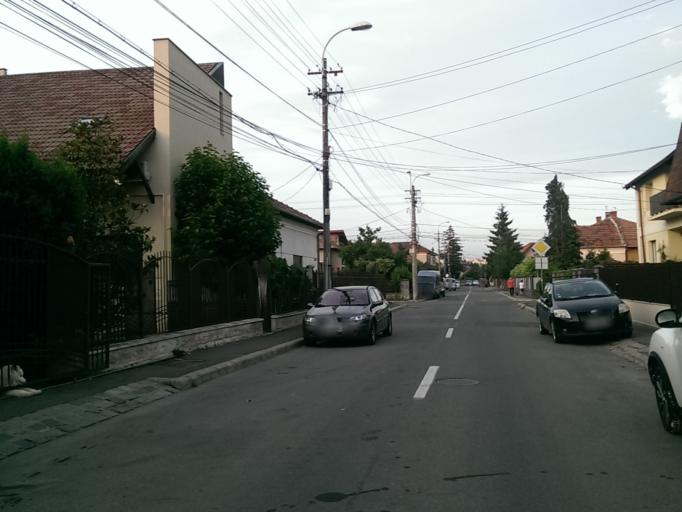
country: RO
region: Cluj
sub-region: Municipiul Cluj-Napoca
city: Cluj-Napoca
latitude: 46.7661
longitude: 23.6081
